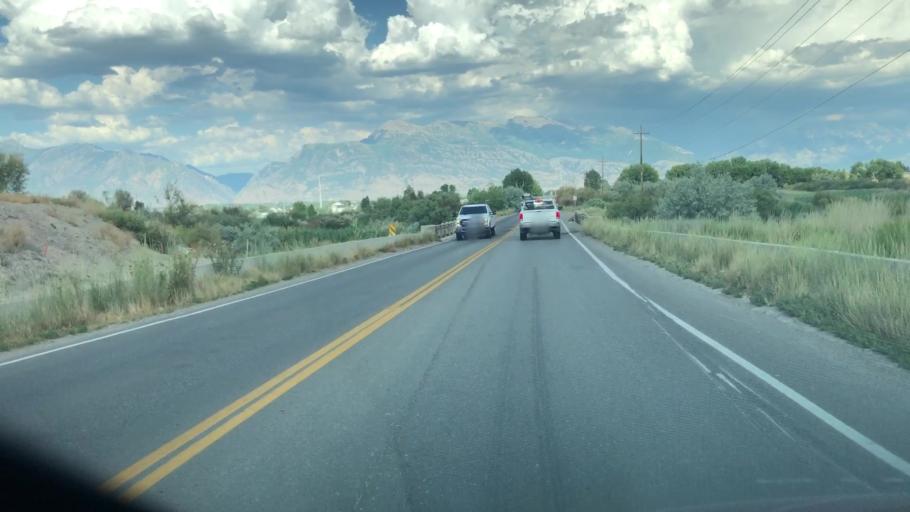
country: US
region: Utah
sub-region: Utah County
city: Saratoga Springs
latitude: 40.3874
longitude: -111.9061
